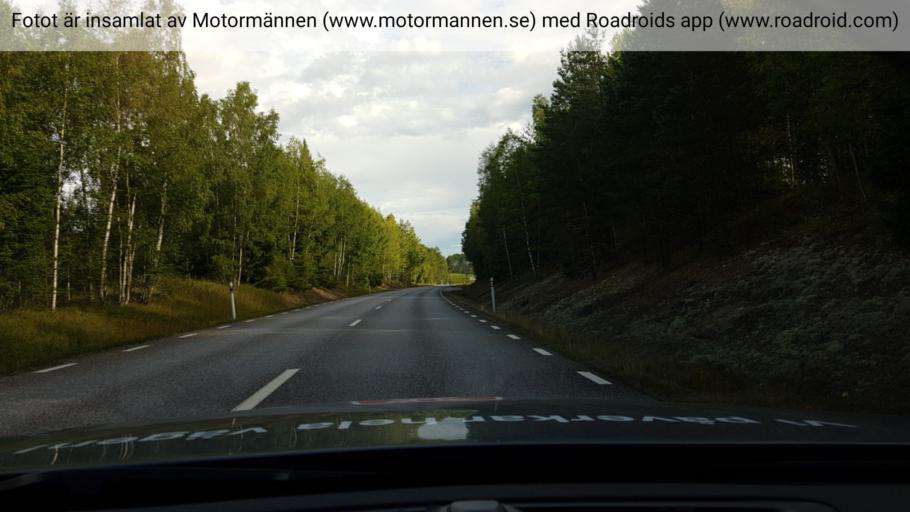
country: SE
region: Uppsala
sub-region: Heby Kommun
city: Morgongava
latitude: 59.8434
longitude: 16.9252
